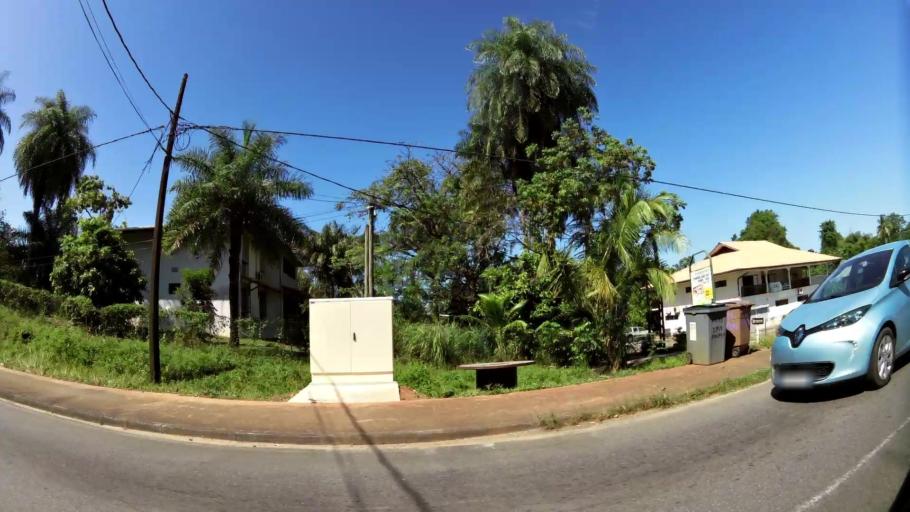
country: GF
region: Guyane
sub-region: Guyane
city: Remire-Montjoly
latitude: 4.9201
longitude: -52.2794
